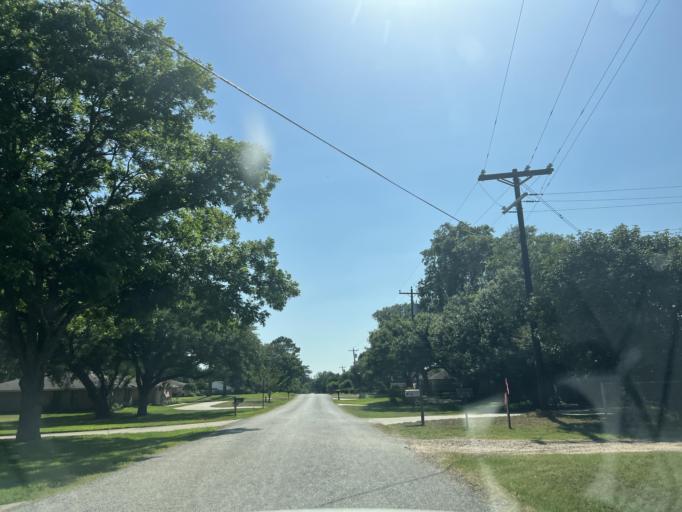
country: US
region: Texas
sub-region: Washington County
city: Brenham
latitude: 30.1534
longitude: -96.3637
